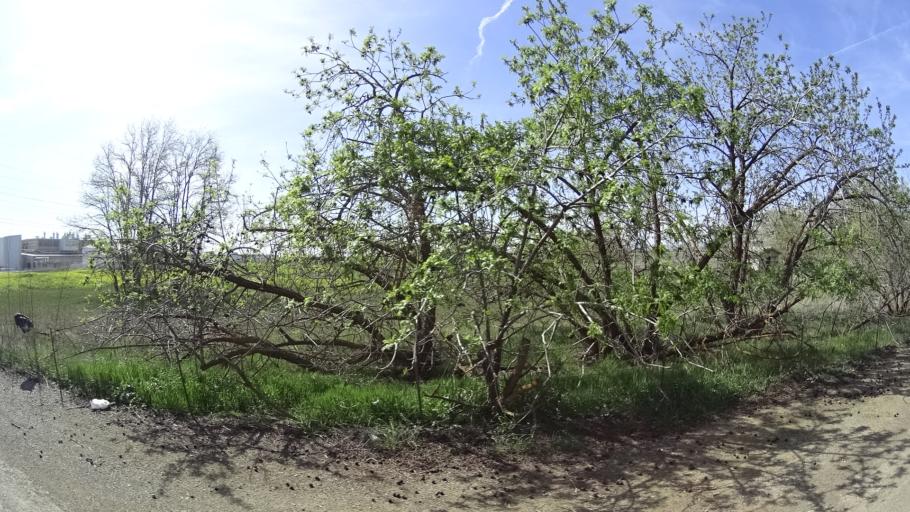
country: US
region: California
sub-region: Glenn County
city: Willows
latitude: 39.5388
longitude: -122.2651
